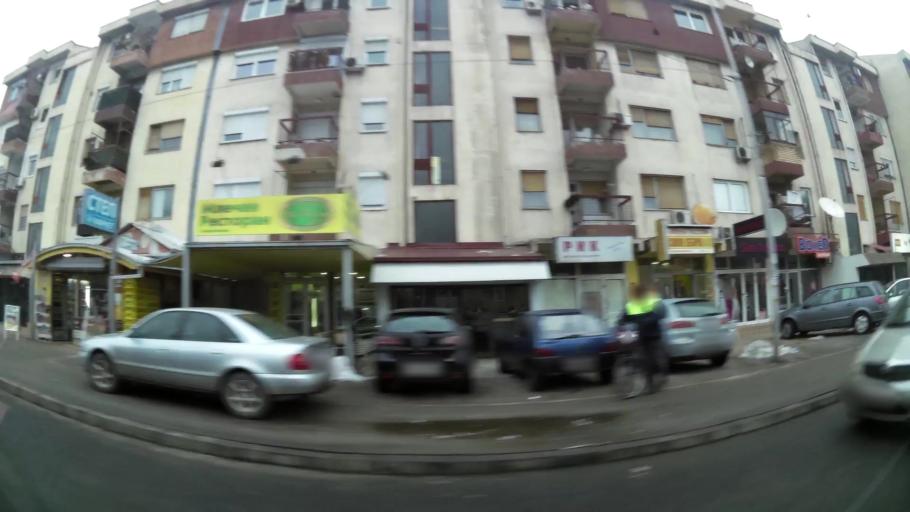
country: MK
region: Saraj
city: Saraj
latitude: 42.0066
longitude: 21.3551
